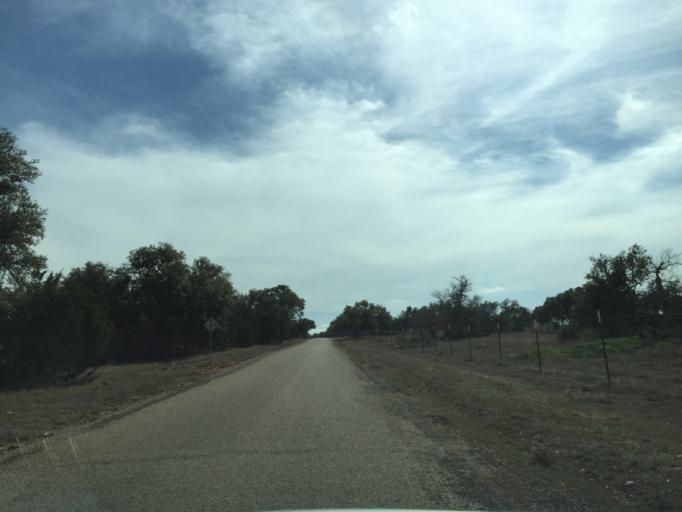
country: US
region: Texas
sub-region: Gillespie County
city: Fredericksburg
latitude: 30.3940
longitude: -98.7066
